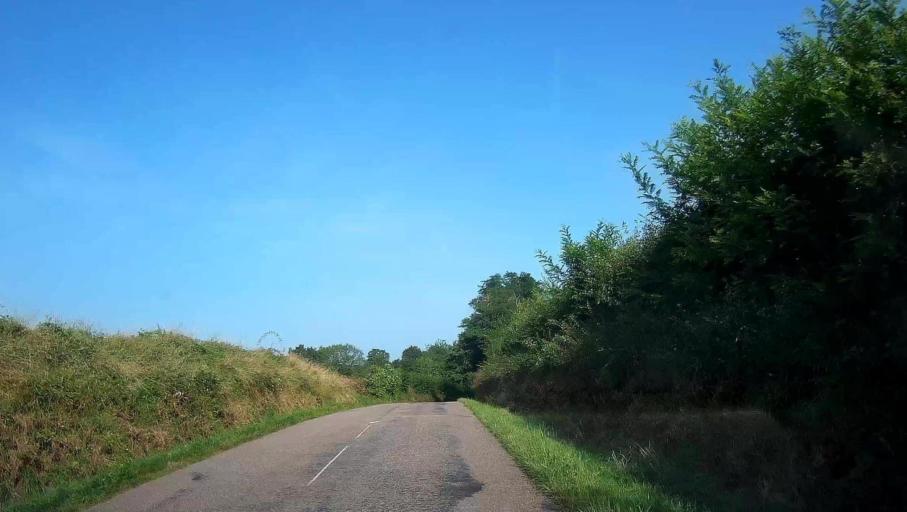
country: FR
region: Bourgogne
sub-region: Departement de Saone-et-Loire
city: Saint-Leger-sur-Dheune
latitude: 46.8715
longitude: 4.6110
